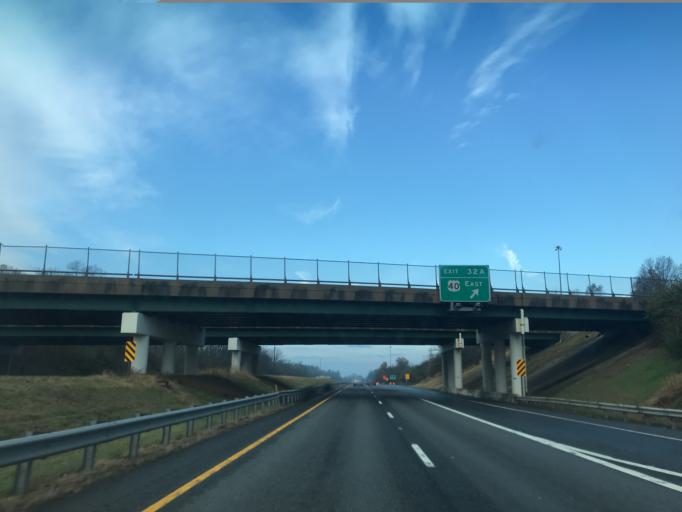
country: US
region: Maryland
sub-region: Washington County
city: Robinwood
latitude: 39.6003
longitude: -77.6816
